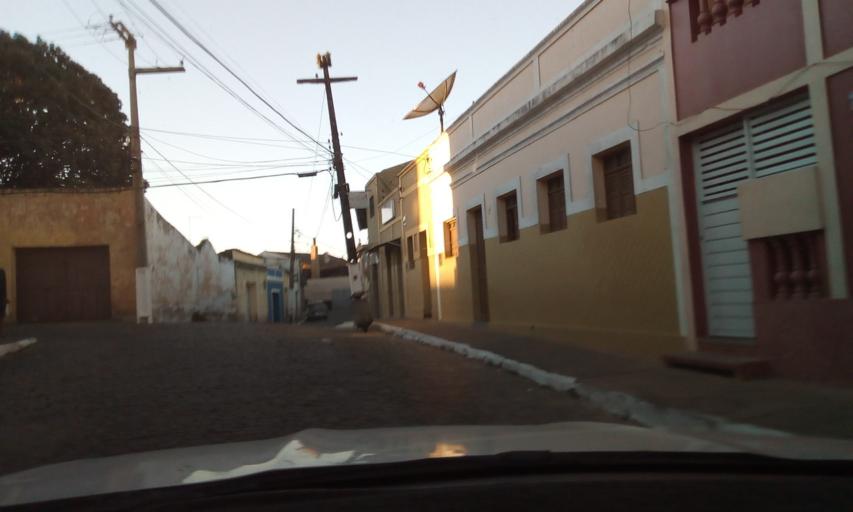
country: BR
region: Paraiba
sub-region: Areia
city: Areia
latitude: -6.9699
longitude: -35.7038
